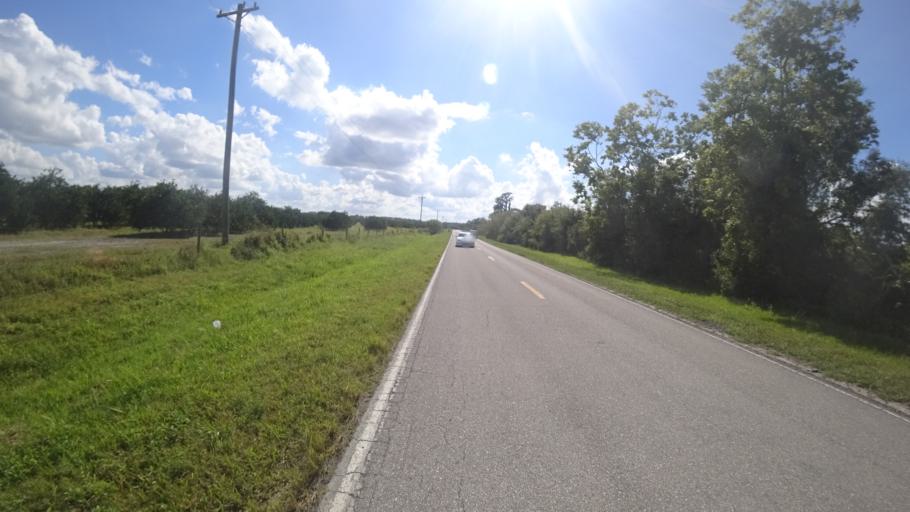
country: US
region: Florida
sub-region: Sarasota County
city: Lake Sarasota
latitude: 27.3969
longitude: -82.1321
